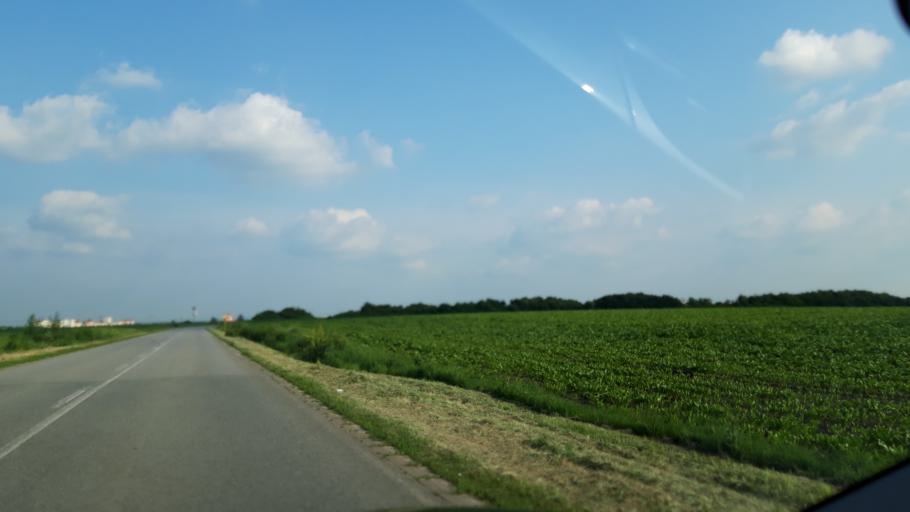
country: RS
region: Autonomna Pokrajina Vojvodina
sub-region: Sremski Okrug
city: Ingija
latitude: 45.0777
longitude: 20.1219
